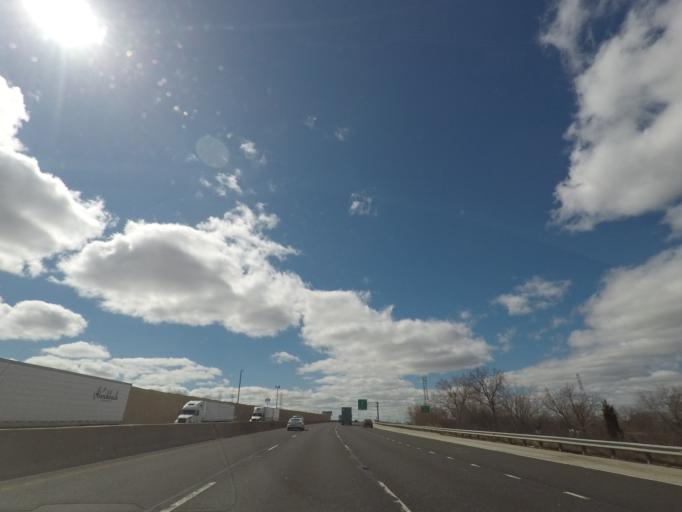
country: US
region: Illinois
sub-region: Will County
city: Crystal Lawns
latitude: 41.5918
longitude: -88.1632
